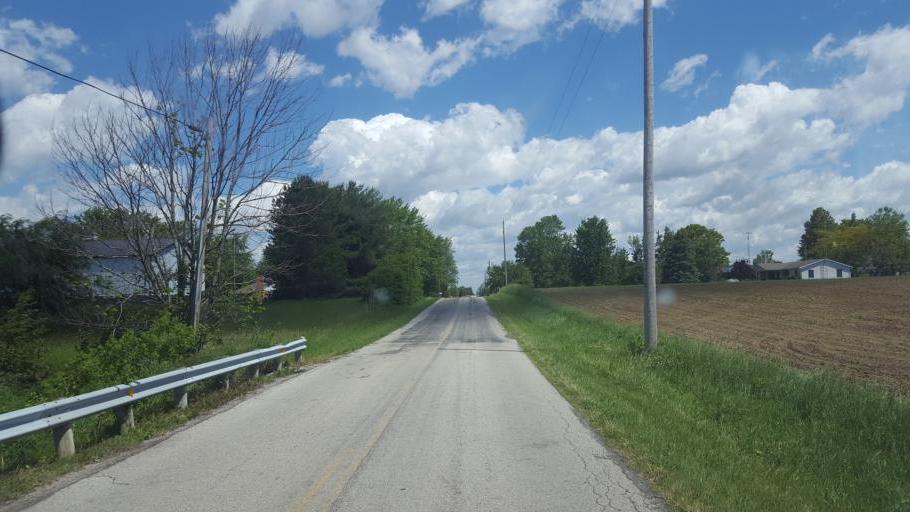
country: US
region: Ohio
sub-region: Richland County
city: Shelby
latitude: 40.8381
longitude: -82.6774
